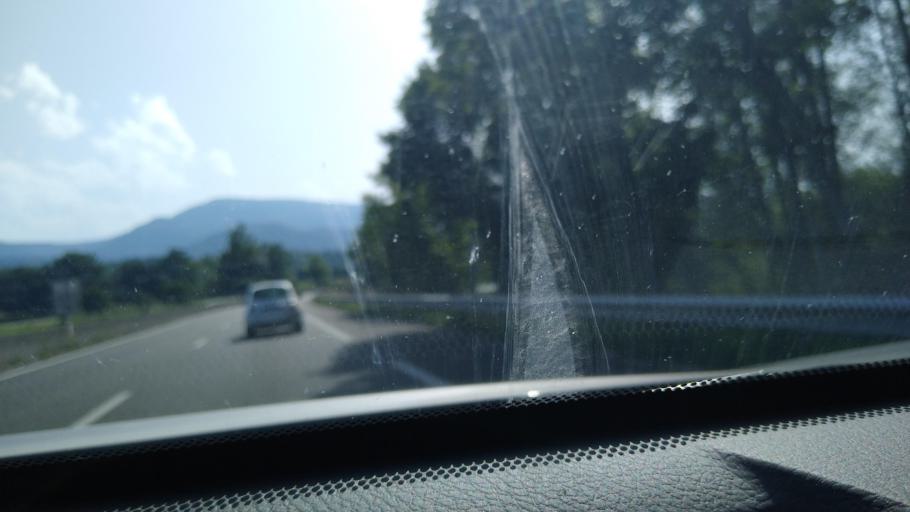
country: FR
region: Midi-Pyrenees
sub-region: Departement de l'Ariege
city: Saint-Lizier
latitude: 43.0372
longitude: 1.0568
